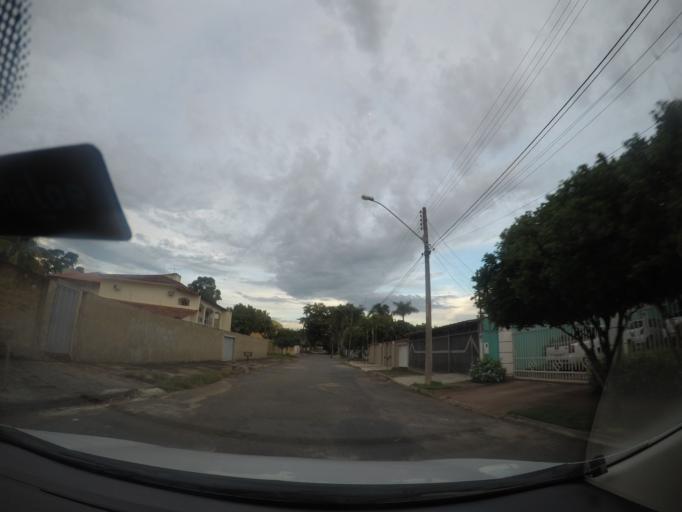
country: BR
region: Goias
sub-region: Goiania
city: Goiania
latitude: -16.6515
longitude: -49.2272
